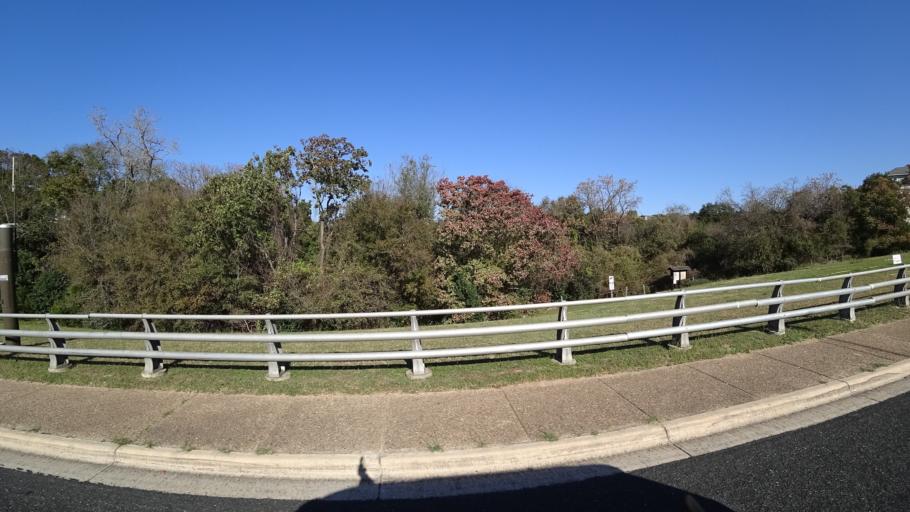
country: US
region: Texas
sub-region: Williamson County
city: Jollyville
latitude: 30.4076
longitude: -97.7540
